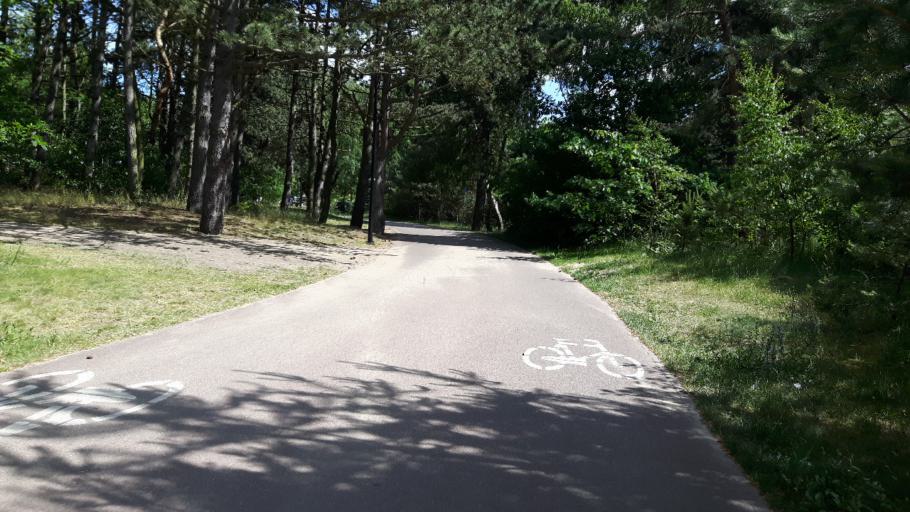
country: PL
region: Pomeranian Voivodeship
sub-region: Gdansk
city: Gdansk
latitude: 54.4121
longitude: 18.6261
